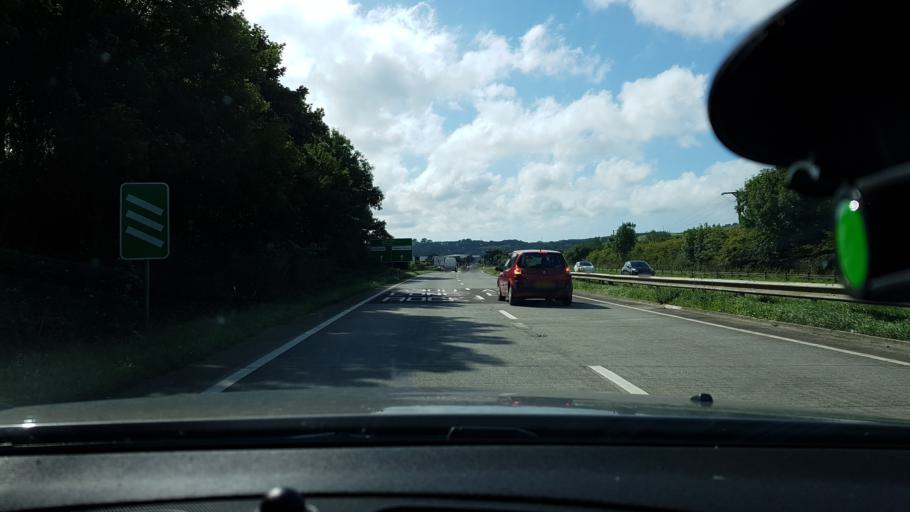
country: GB
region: England
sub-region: Cornwall
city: Penzance
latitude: 50.1304
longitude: -5.5084
